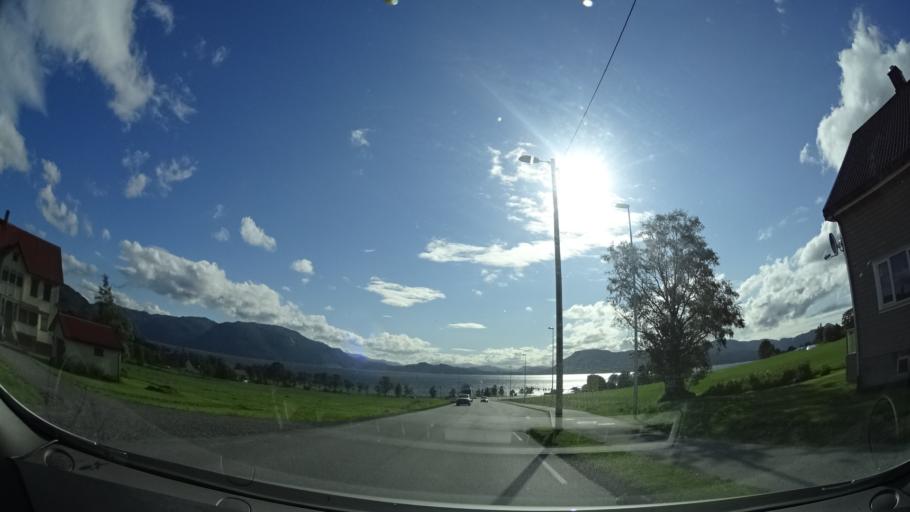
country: NO
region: More og Romsdal
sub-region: Halsa
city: Liaboen
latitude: 63.0689
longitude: 8.2382
